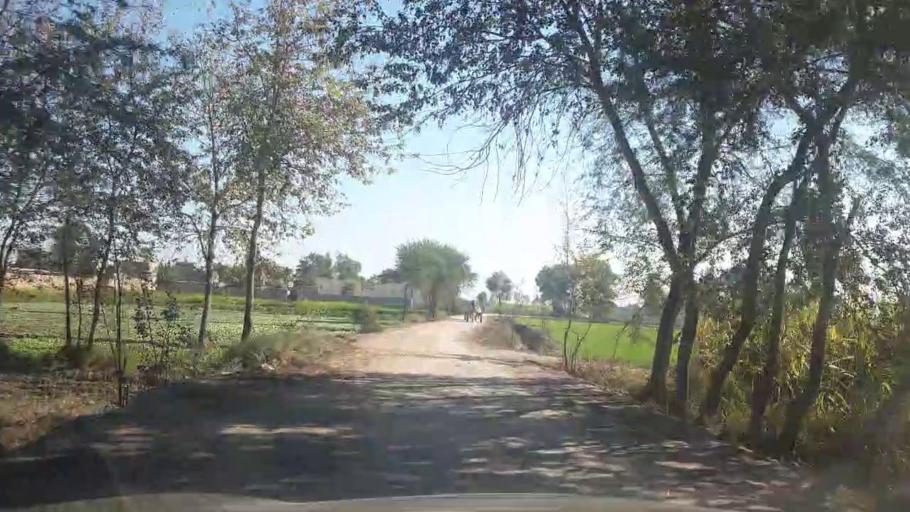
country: PK
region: Sindh
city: Adilpur
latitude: 27.9699
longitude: 69.3316
